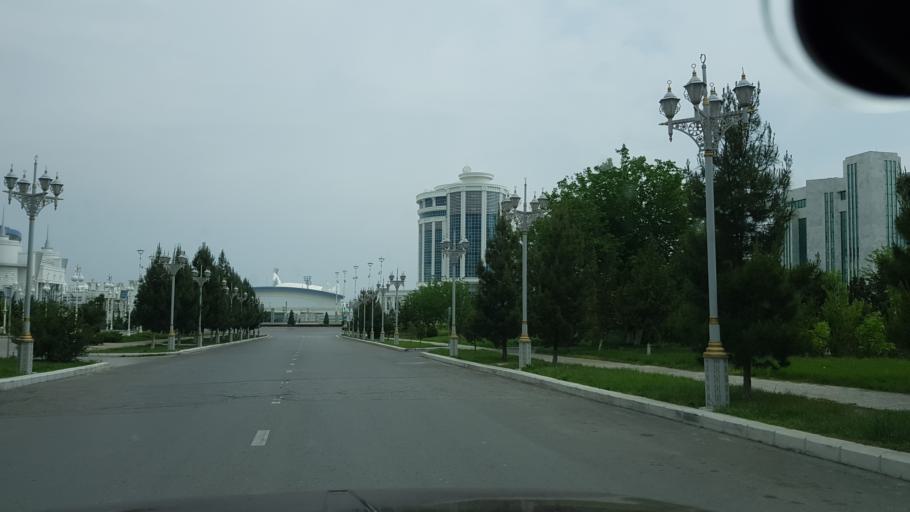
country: TM
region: Ahal
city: Ashgabat
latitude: 37.8940
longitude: 58.3770
